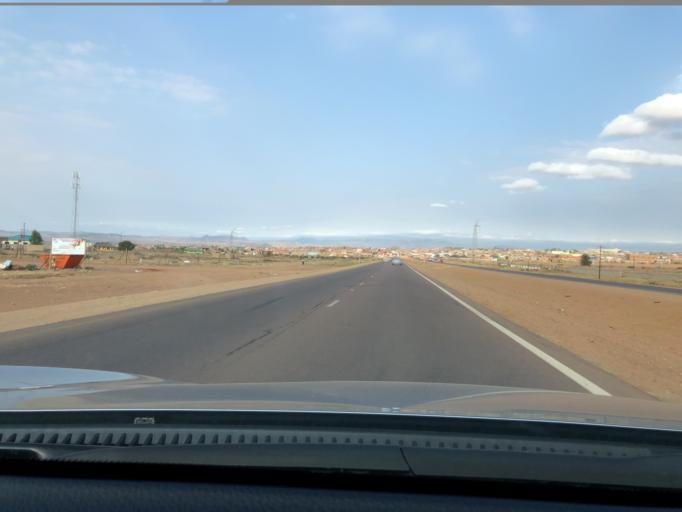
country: ZA
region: Limpopo
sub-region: Capricorn District Municipality
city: Mankoeng
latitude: -23.8875
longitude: 29.6803
